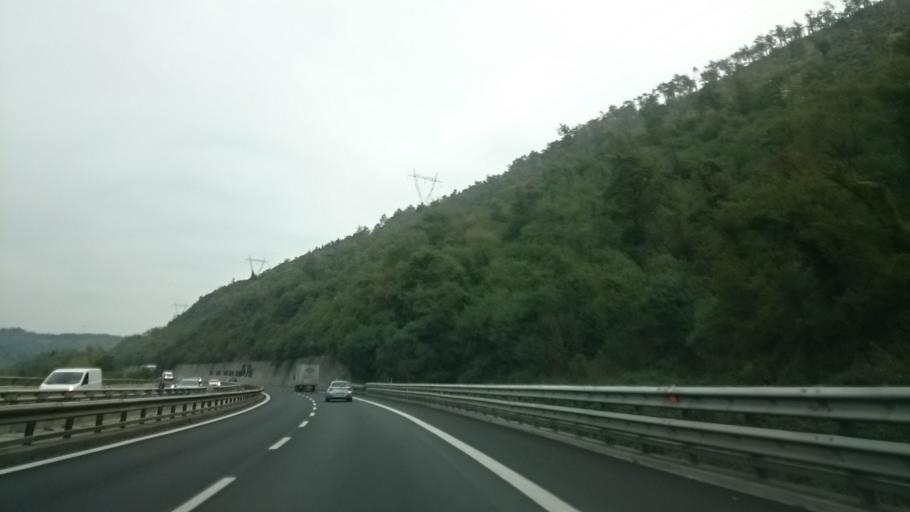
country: IT
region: Tuscany
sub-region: Province of Florence
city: Carraia
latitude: 43.9260
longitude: 11.2172
